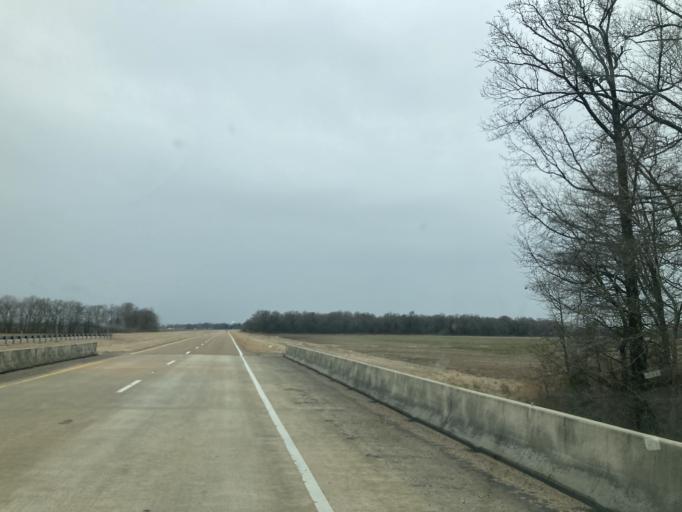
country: US
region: Mississippi
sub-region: Humphreys County
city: Belzoni
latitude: 33.0768
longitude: -90.4781
